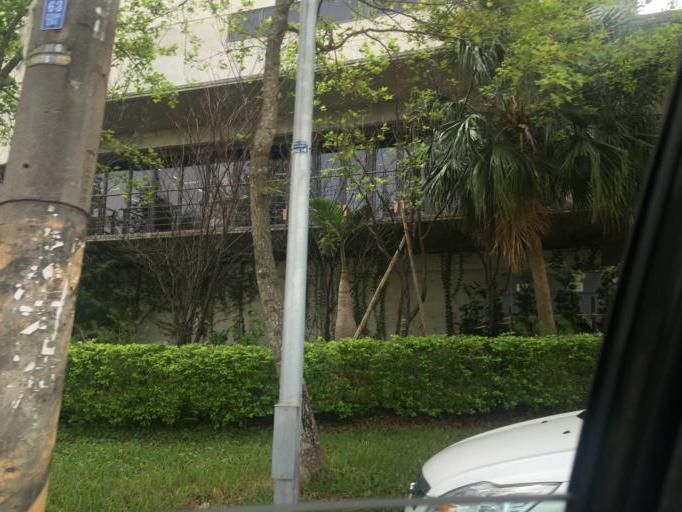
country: TW
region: Taiwan
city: Daxi
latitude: 24.8403
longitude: 121.2107
